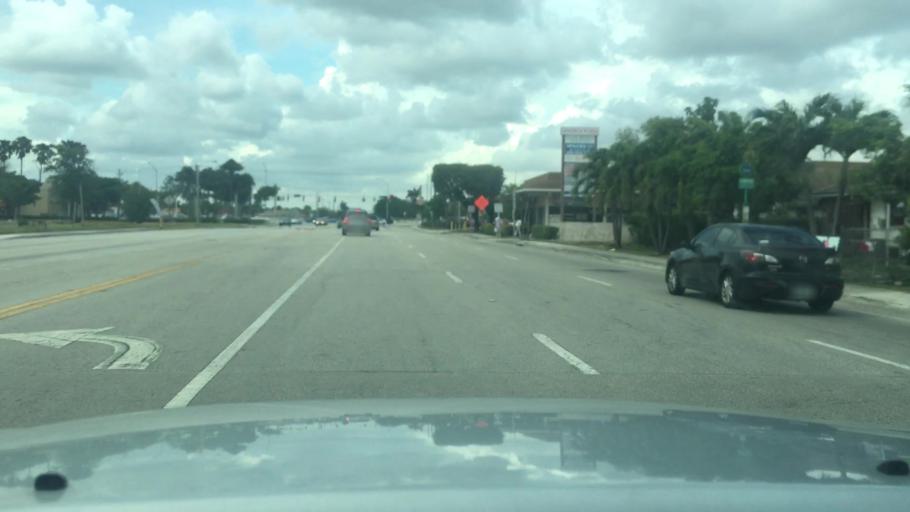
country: US
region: Florida
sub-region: Miami-Dade County
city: Tamiami
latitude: 25.7590
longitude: -80.3927
